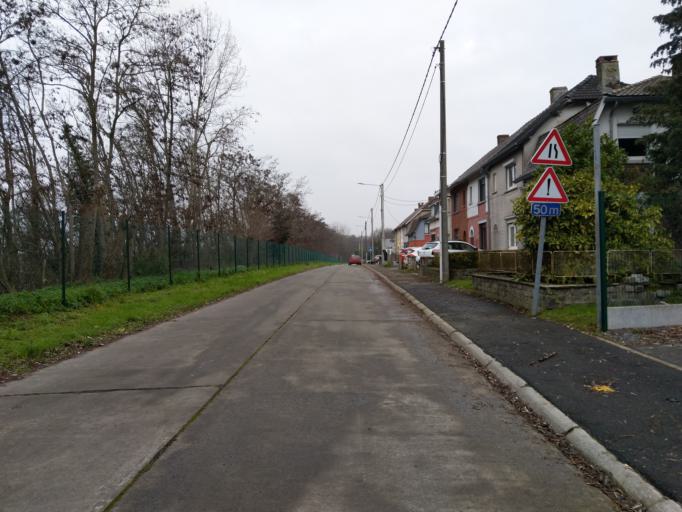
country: BE
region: Wallonia
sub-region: Province du Hainaut
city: Mons
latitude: 50.4809
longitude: 4.0049
